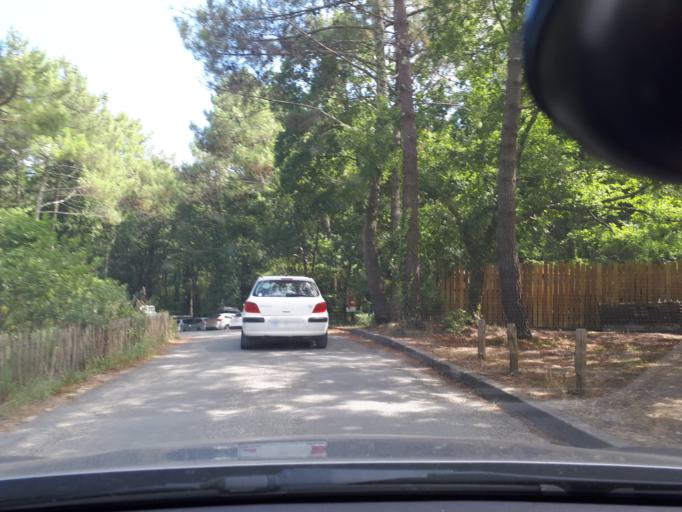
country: FR
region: Aquitaine
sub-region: Departement de la Gironde
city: Arcachon
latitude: 44.5968
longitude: -1.1980
